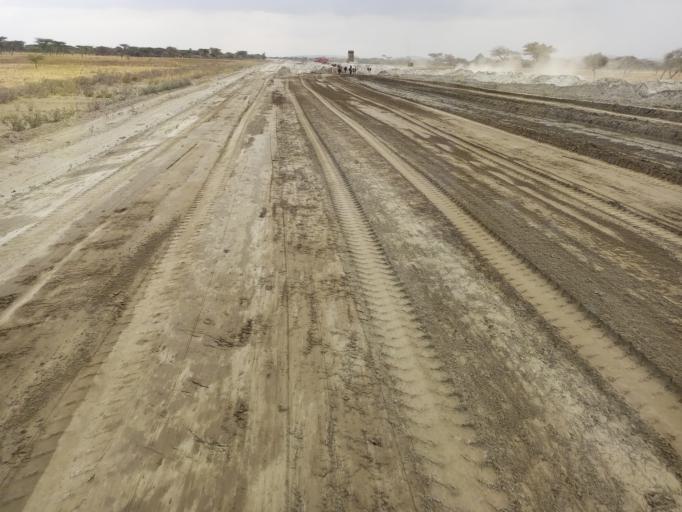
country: ET
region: Oromiya
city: Ziway
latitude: 7.9110
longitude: 38.6815
